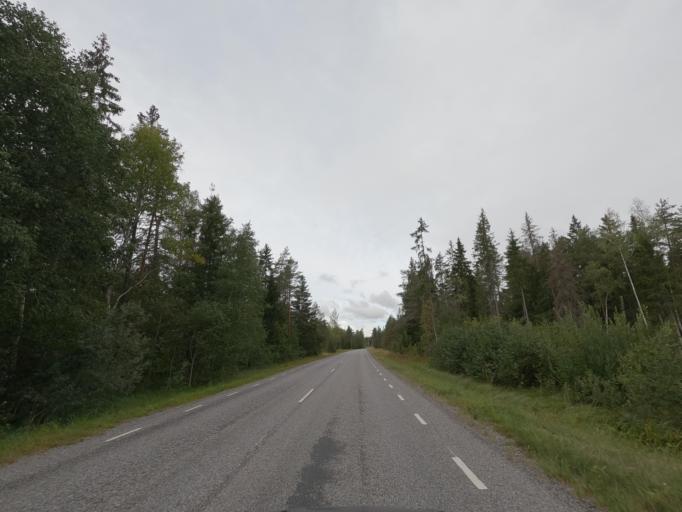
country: EE
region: Raplamaa
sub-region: Rapla vald
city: Rapla
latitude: 59.0049
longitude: 24.6262
